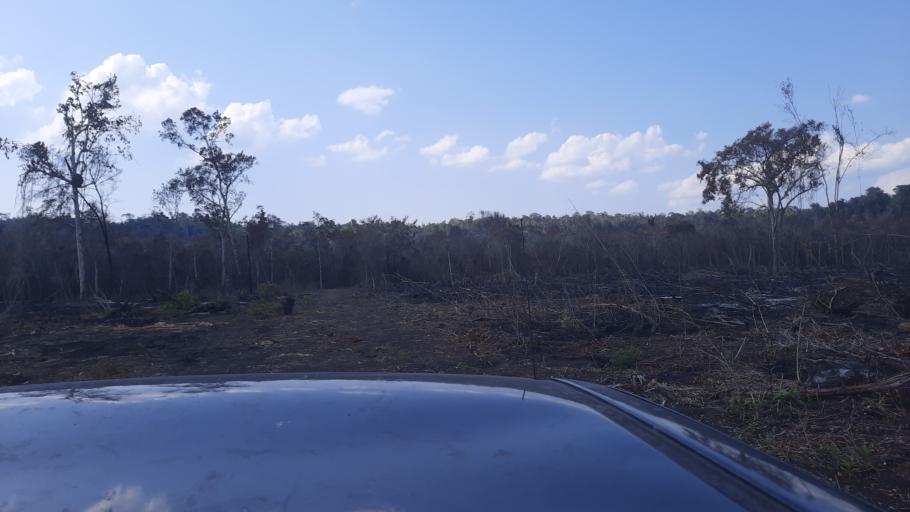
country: BZ
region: Cayo
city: Valley of Peace
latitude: 17.4045
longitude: -89.0366
